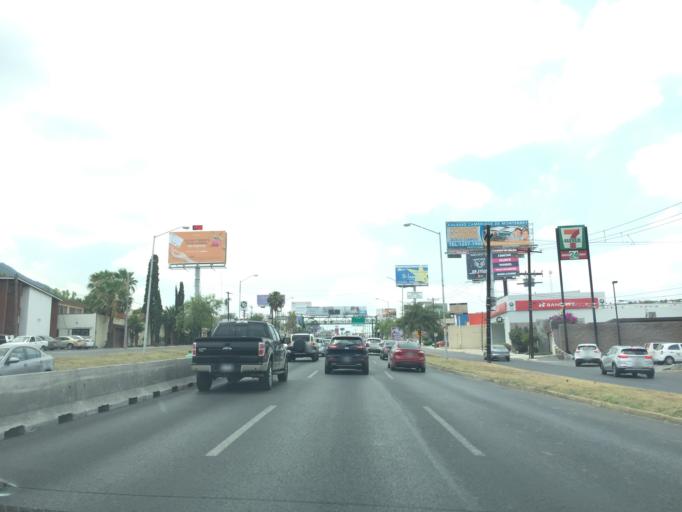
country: MX
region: Nuevo Leon
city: Garza Garcia
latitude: 25.7092
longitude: -100.3741
